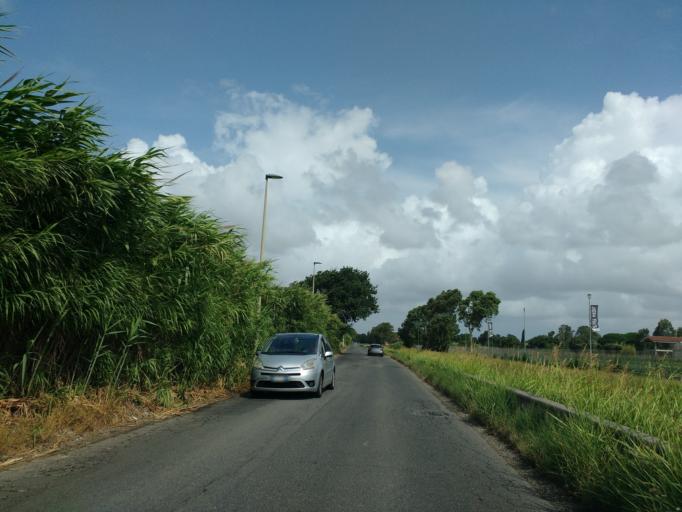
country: IT
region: Latium
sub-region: Citta metropolitana di Roma Capitale
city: Acilia-Castel Fusano-Ostia Antica
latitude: 41.7622
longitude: 12.3285
